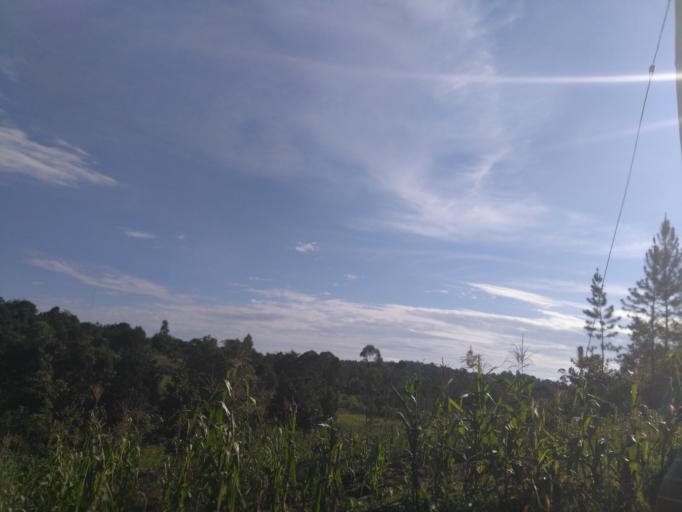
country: UG
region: Eastern Region
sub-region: Jinja District
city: Jinja
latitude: 0.4632
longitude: 33.1818
